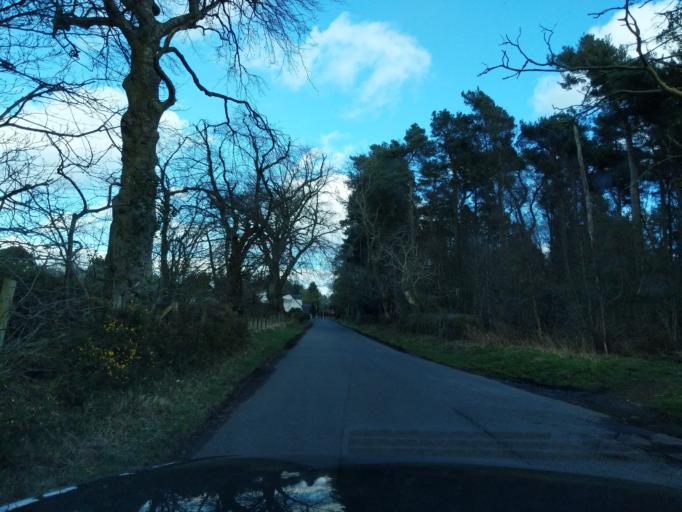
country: GB
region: Scotland
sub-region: Edinburgh
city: Balerno
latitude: 55.8797
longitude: -3.3540
